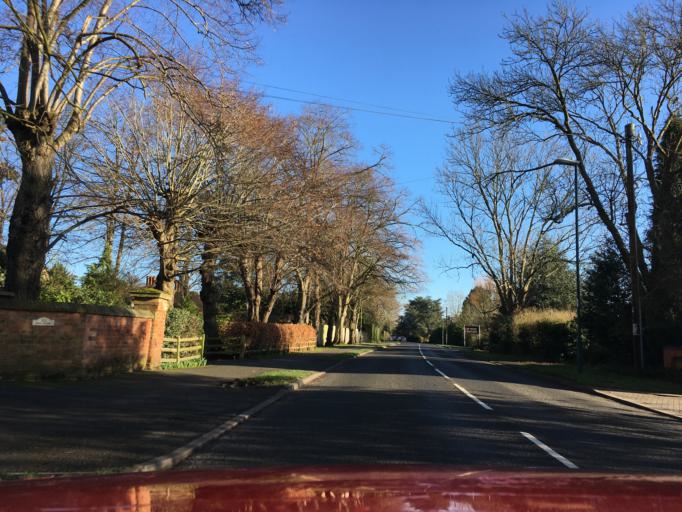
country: GB
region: England
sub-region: Warwickshire
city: Stratford-upon-Avon
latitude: 52.1949
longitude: -1.6919
